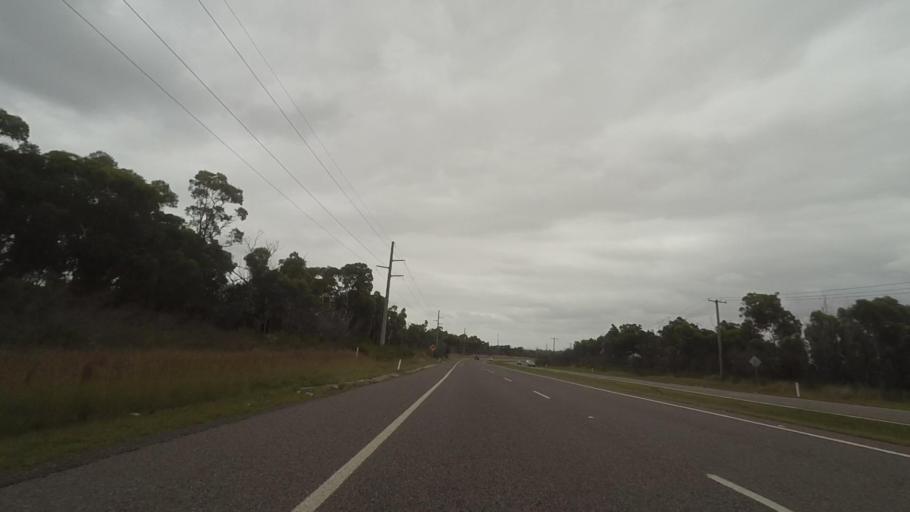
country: AU
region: New South Wales
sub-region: Wyong Shire
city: Kingfisher Shores
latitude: -33.1830
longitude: 151.5922
